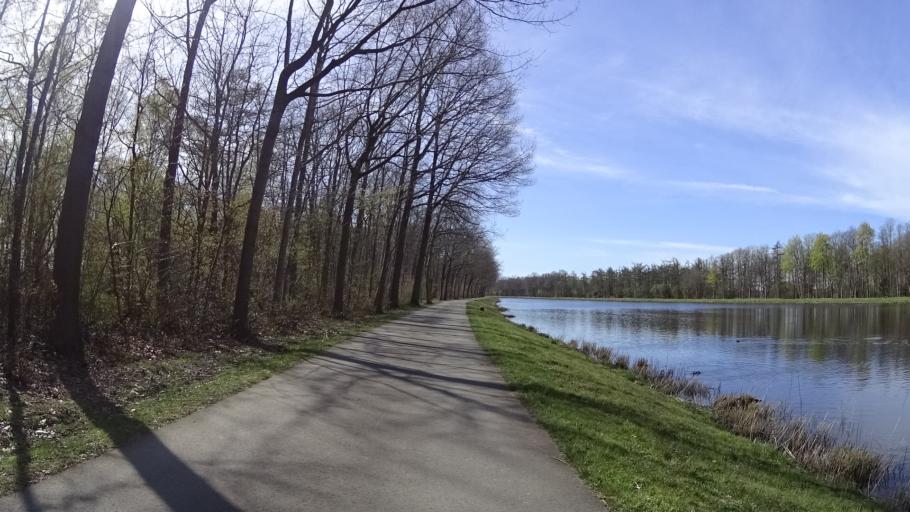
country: DE
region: Lower Saxony
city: Geeste
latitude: 52.6177
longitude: 7.3087
